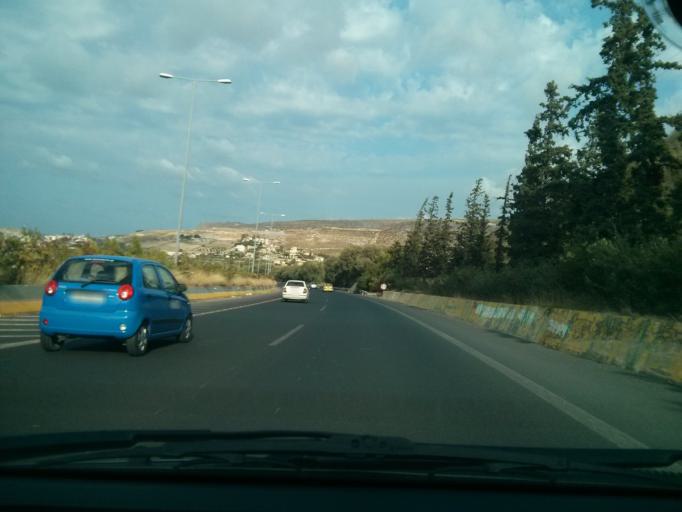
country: GR
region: Crete
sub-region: Nomos Irakleiou
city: Nea Alikarnassos
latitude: 35.3210
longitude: 25.1893
